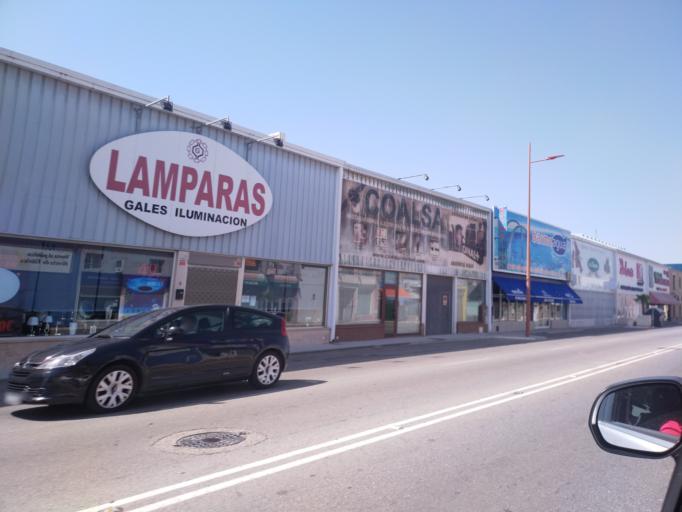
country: ES
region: Andalusia
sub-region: Provincia de Cadiz
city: Chiclana de la Frontera
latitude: 36.4266
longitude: -6.1523
